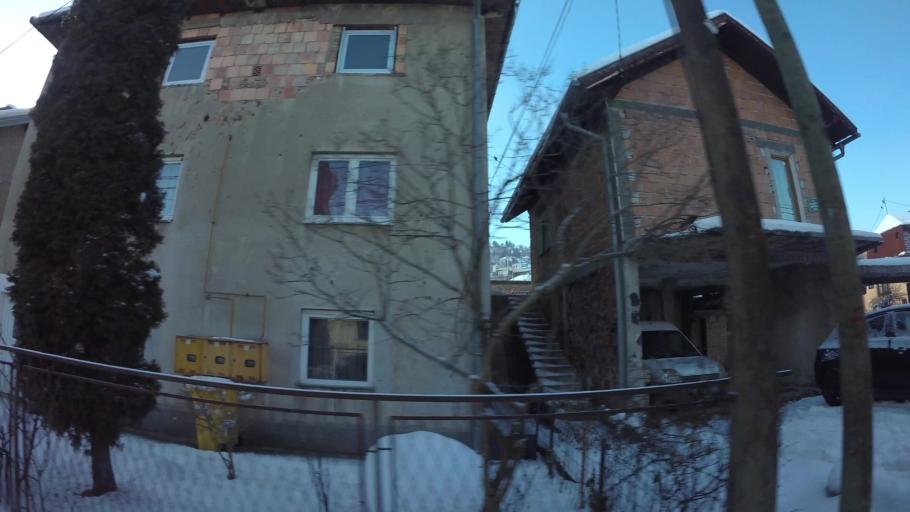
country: BA
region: Federation of Bosnia and Herzegovina
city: Kobilja Glava
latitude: 43.8821
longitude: 18.3893
